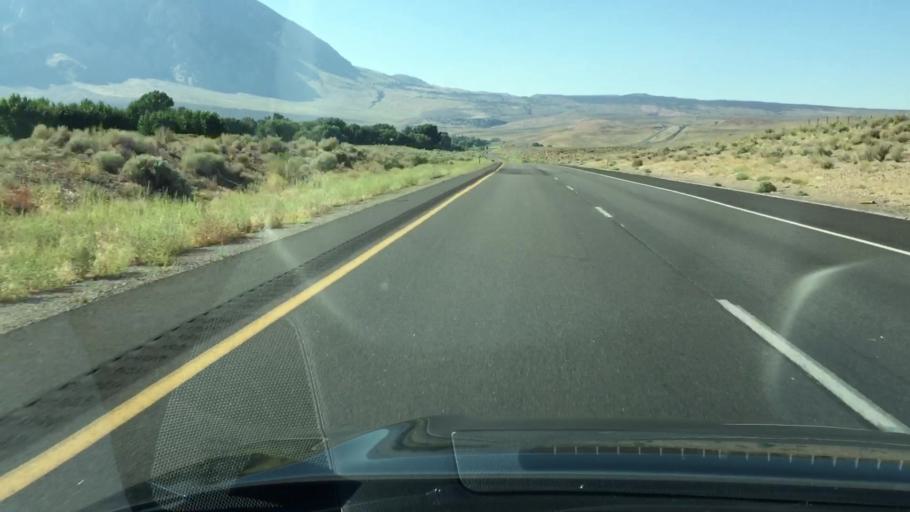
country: US
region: California
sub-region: Inyo County
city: West Bishop
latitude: 37.4265
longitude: -118.5597
